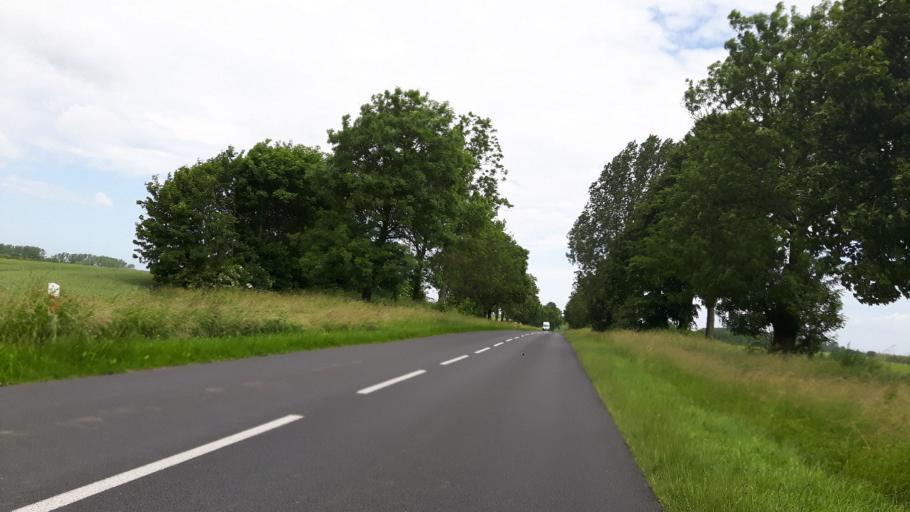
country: PL
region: West Pomeranian Voivodeship
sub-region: Powiat gryficki
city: Trzebiatow
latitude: 54.0257
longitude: 15.2411
